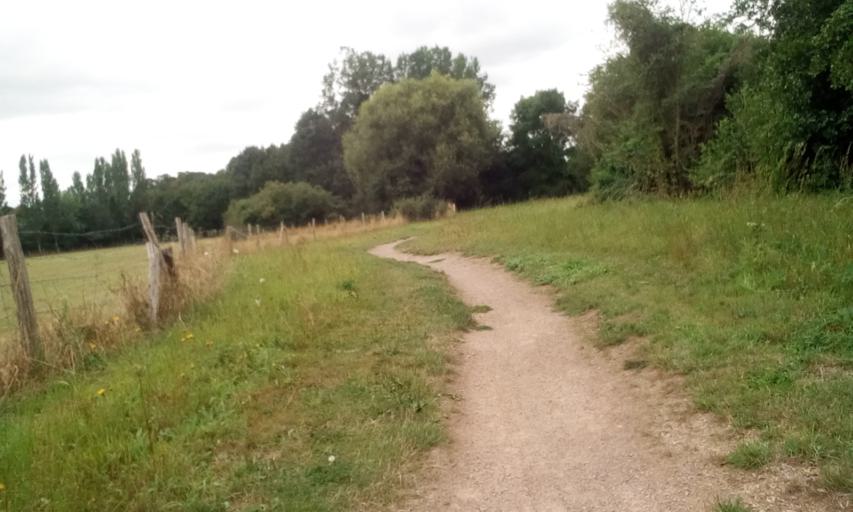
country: FR
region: Lower Normandy
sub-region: Departement du Calvados
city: Bretteville-sur-Odon
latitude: 49.1596
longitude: -0.4321
